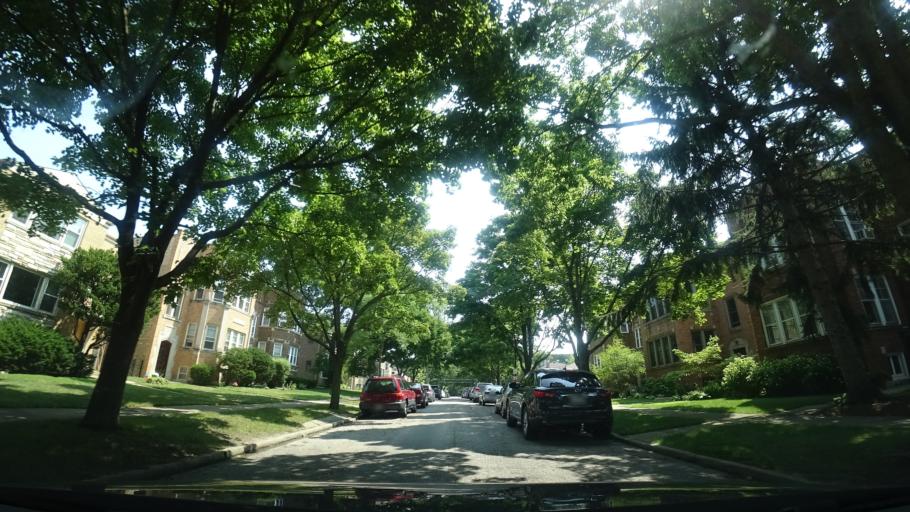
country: US
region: Illinois
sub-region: Cook County
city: Evanston
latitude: 42.0290
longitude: -87.6922
